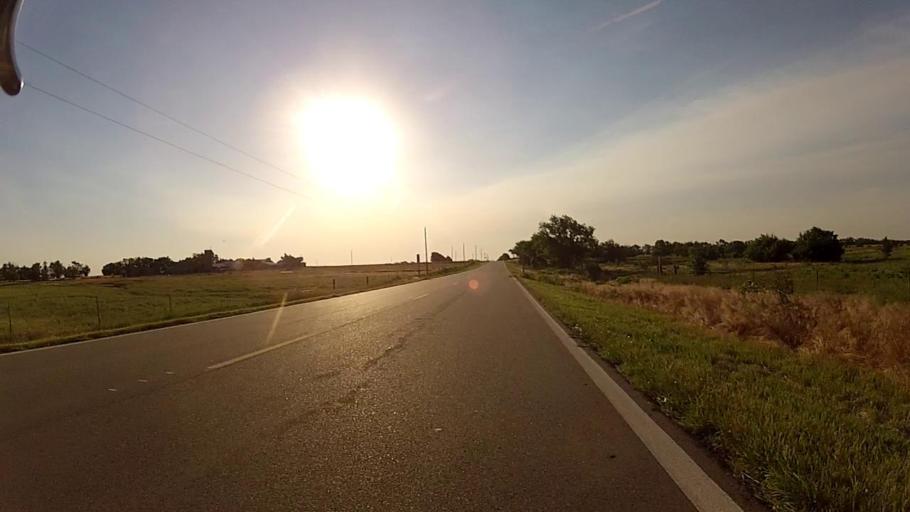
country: US
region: Kansas
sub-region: Sumner County
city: Caldwell
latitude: 37.1544
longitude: -97.7881
